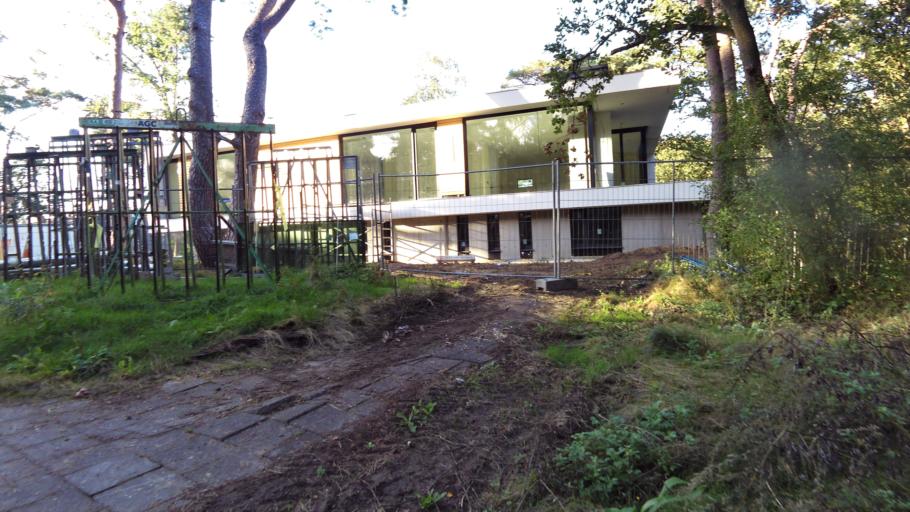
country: NL
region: Utrecht
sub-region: Gemeente Zeist
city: Zeist
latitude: 52.1241
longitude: 5.2175
